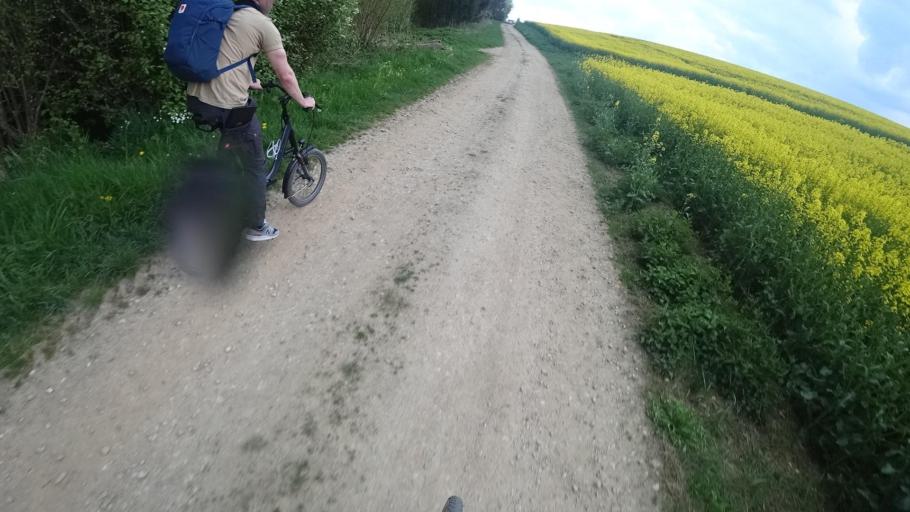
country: DE
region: Rheinland-Pfalz
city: Pleizenhausen
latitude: 50.0015
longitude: 7.5581
